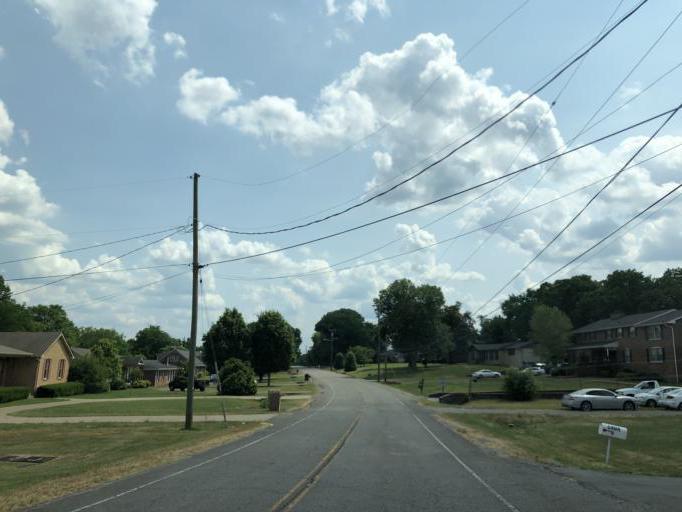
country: US
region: Tennessee
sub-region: Davidson County
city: Goodlettsville
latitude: 36.2441
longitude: -86.7297
